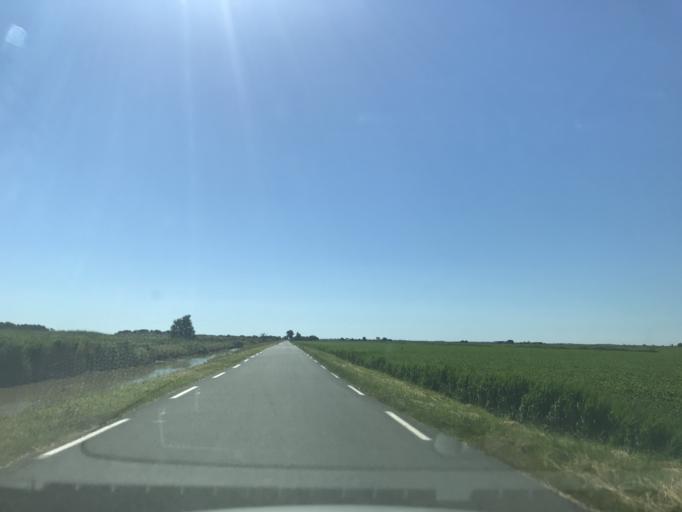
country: FR
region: Aquitaine
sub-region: Departement de la Gironde
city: Braud-et-Saint-Louis
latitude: 45.2867
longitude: -0.6796
